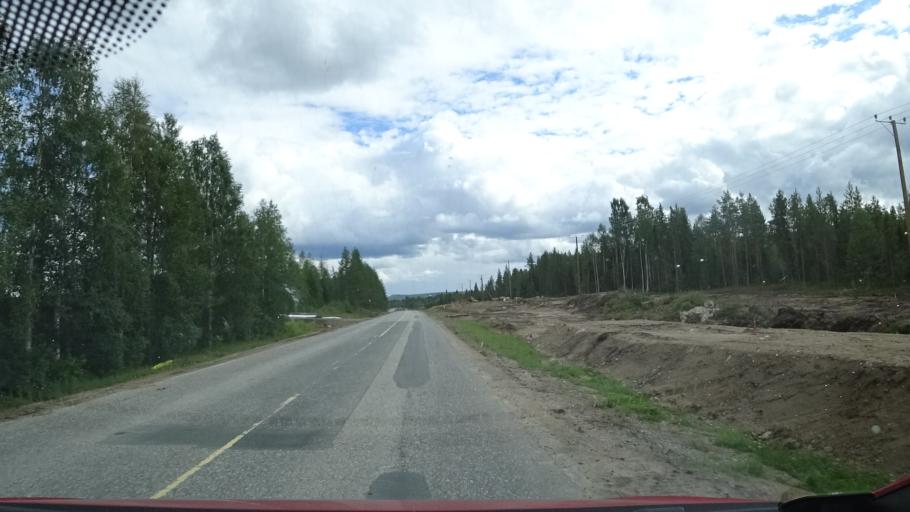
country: FI
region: Lapland
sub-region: Rovaniemi
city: Rovaniemi
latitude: 66.5424
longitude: 25.7137
